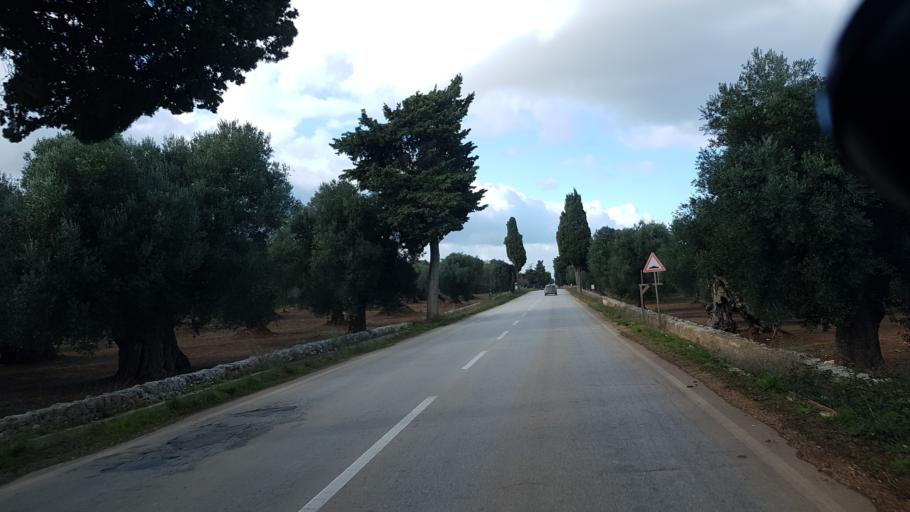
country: IT
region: Apulia
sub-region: Provincia di Brindisi
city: Montalbano
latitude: 40.7747
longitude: 17.4975
